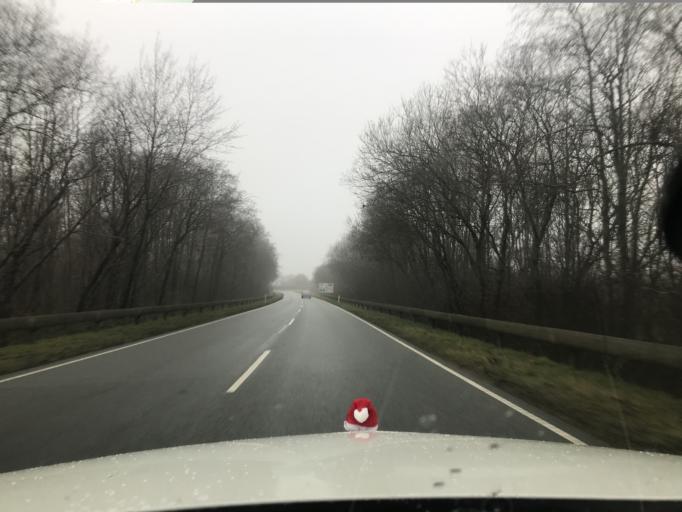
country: DK
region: South Denmark
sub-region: Aabenraa Kommune
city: Aabenraa
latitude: 55.0028
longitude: 9.4241
